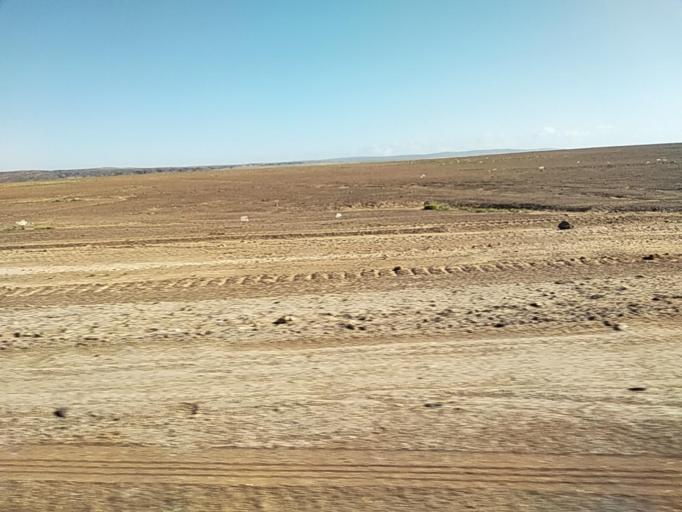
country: CL
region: Atacama
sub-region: Provincia de Copiapo
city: Copiapo
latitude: -27.3224
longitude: -70.8143
